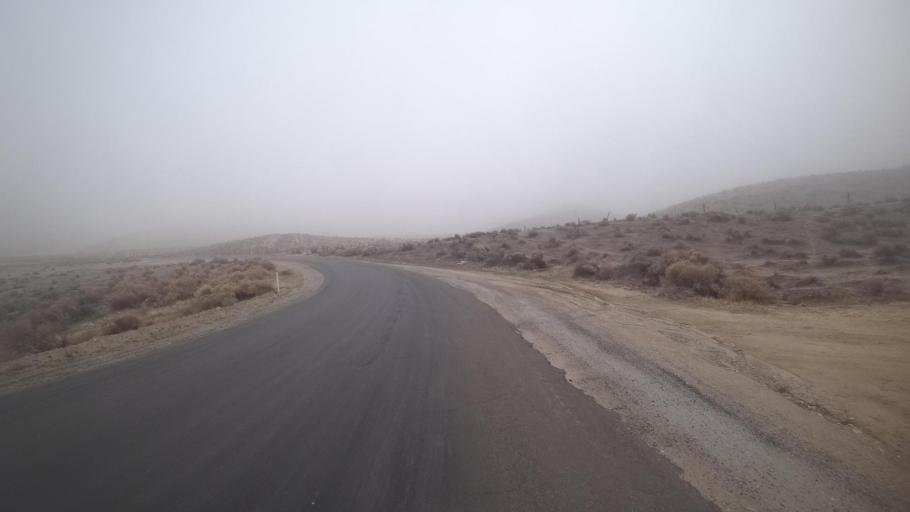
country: US
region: California
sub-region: Kern County
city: Maricopa
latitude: 35.0400
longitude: -119.4248
